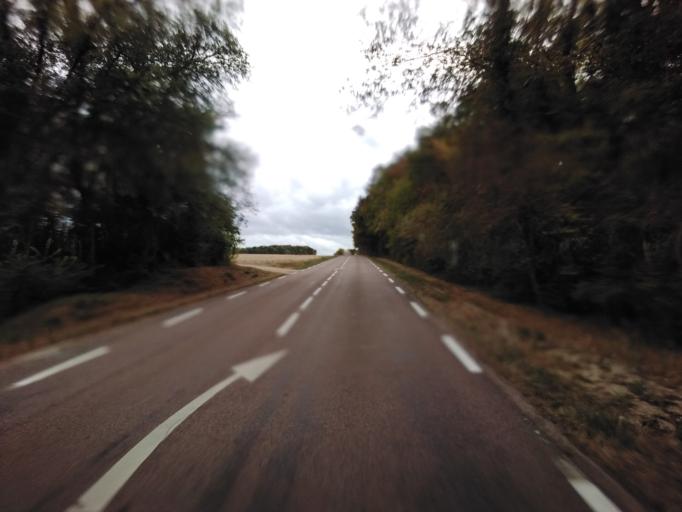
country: FR
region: Champagne-Ardenne
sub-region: Departement de l'Aube
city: Bar-sur-Seine
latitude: 48.1569
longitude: 4.4118
